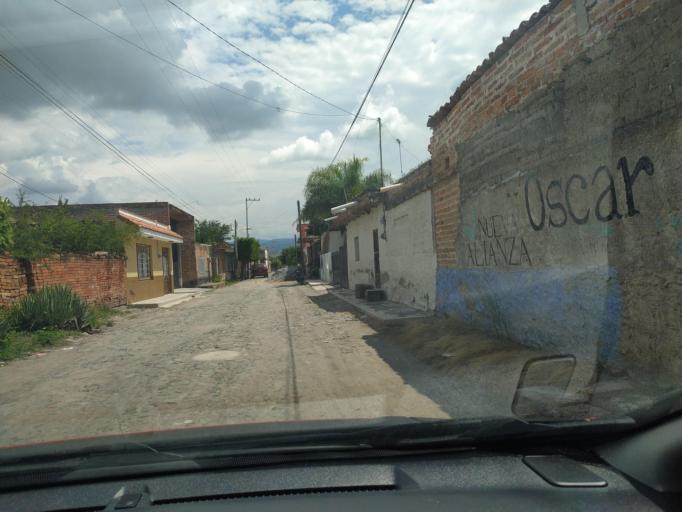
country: MX
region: Jalisco
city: Villa Corona
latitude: 20.3482
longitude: -103.6715
